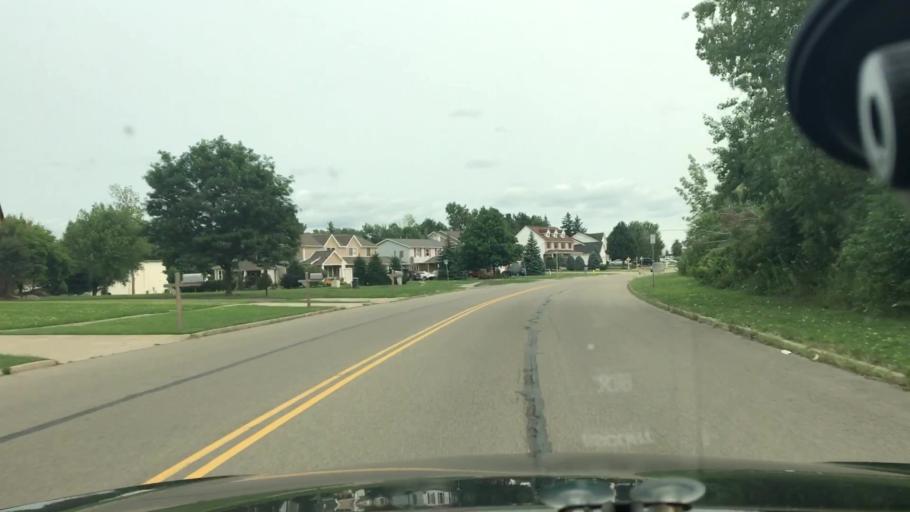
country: US
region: New York
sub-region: Erie County
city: Blasdell
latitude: 42.7779
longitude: -78.8065
